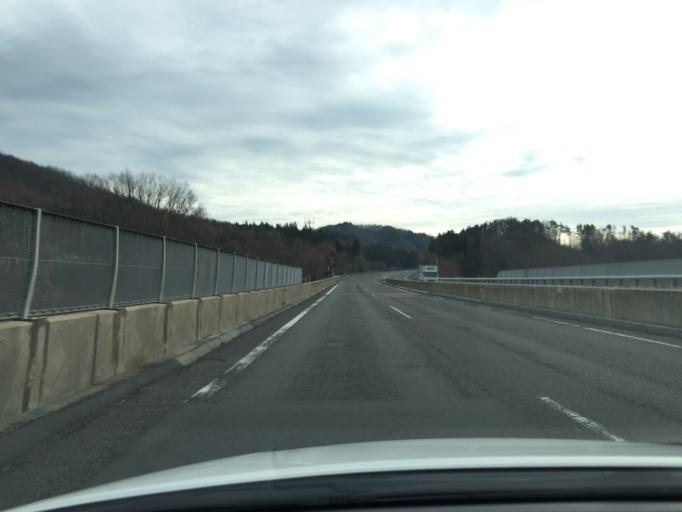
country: JP
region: Fukushima
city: Funehikimachi-funehiki
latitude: 37.4247
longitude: 140.5541
